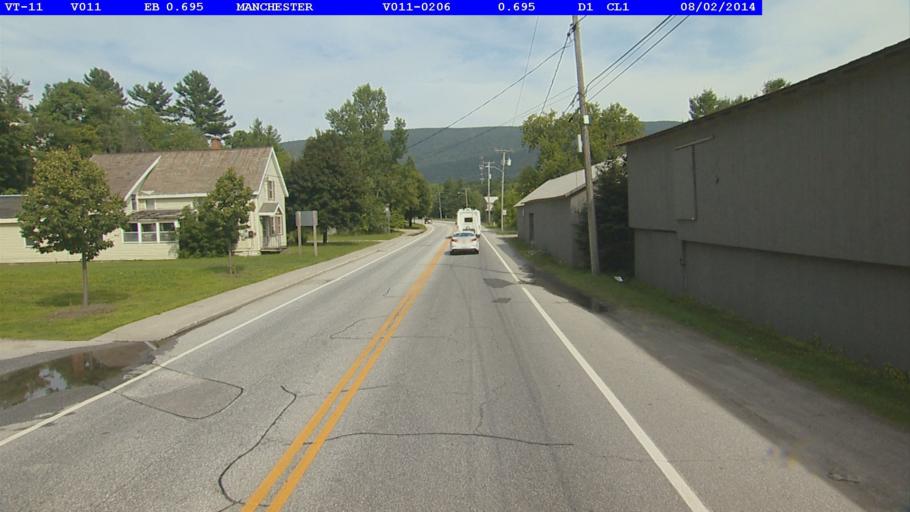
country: US
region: Vermont
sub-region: Bennington County
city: Manchester Center
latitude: 43.1724
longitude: -73.0448
